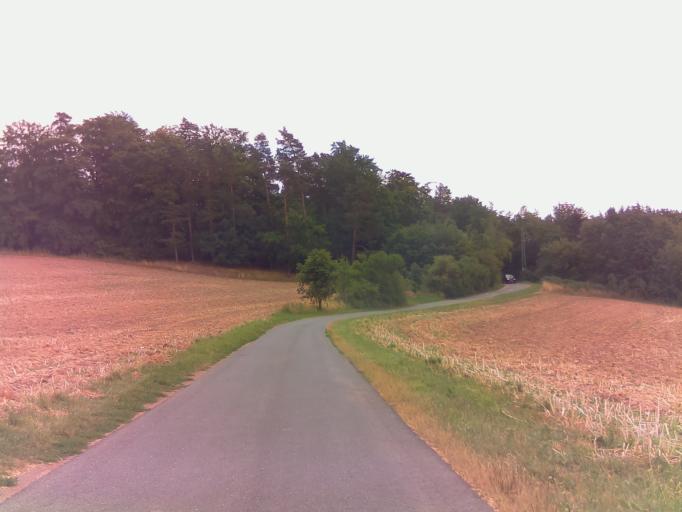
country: DE
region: Thuringia
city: Gosswitz
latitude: 50.6296
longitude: 11.4941
